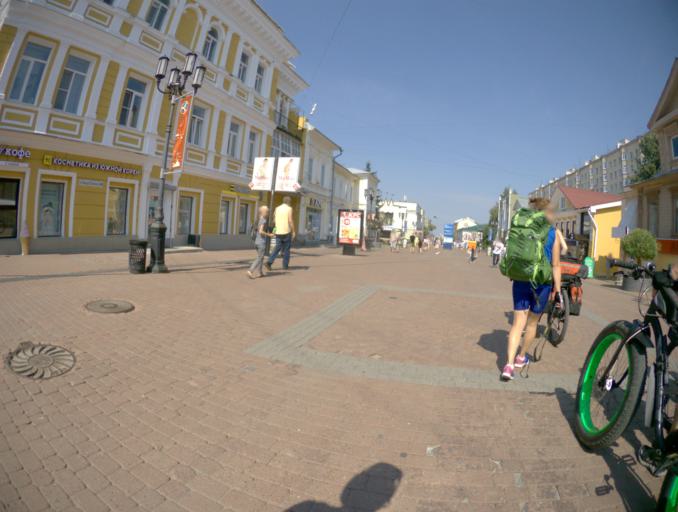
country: RU
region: Nizjnij Novgorod
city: Nizhniy Novgorod
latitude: 56.3174
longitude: 43.9951
